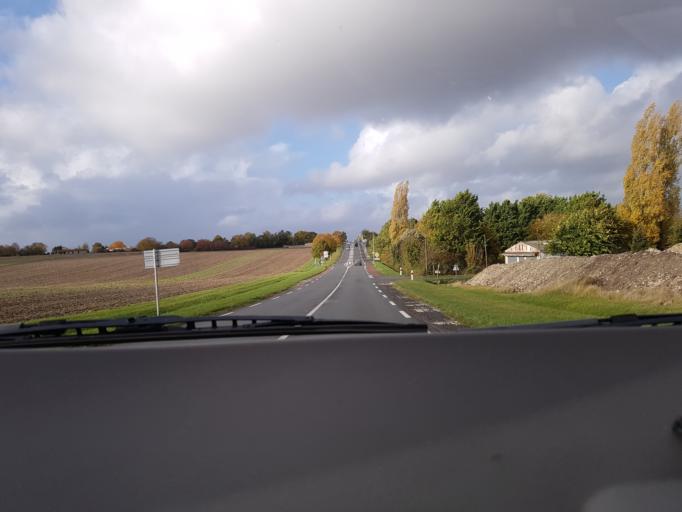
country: FR
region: Poitou-Charentes
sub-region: Departement de la Charente-Maritime
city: Thenac
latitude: 45.6488
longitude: -0.5848
